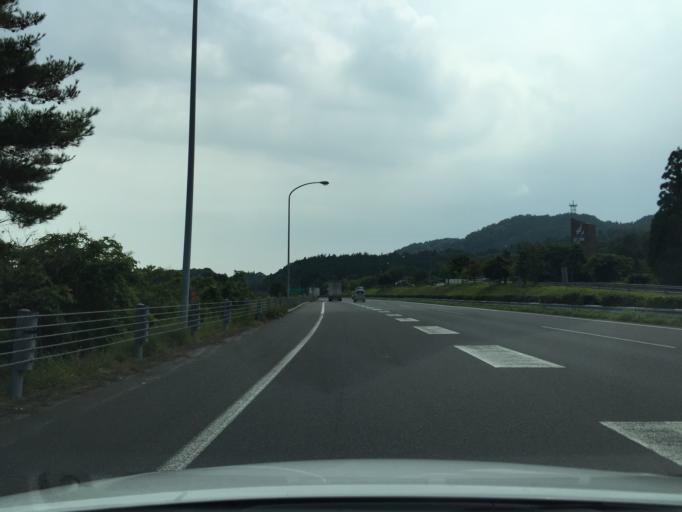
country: JP
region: Fukushima
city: Iwaki
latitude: 37.0218
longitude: 140.8135
